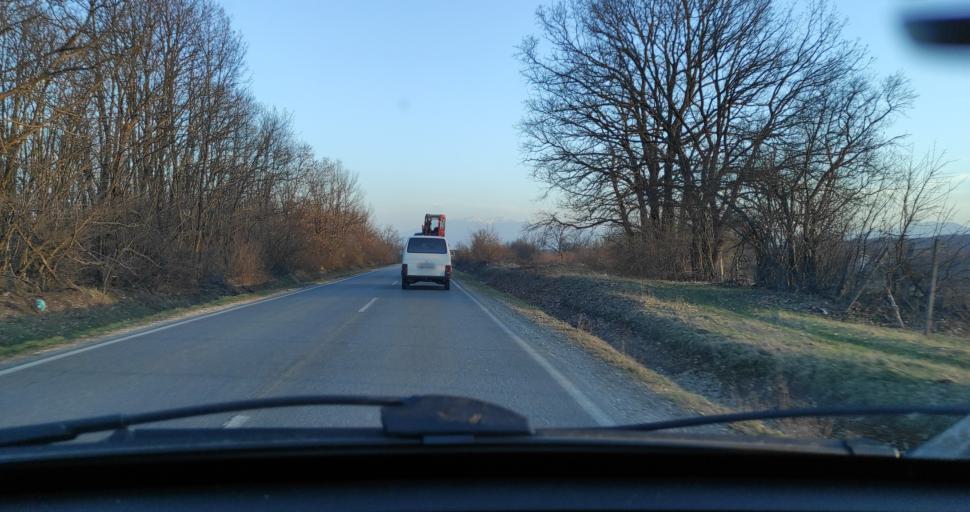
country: XK
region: Gjakova
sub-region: Komuna e Decanit
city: Gllogjan
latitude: 42.4408
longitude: 20.3677
